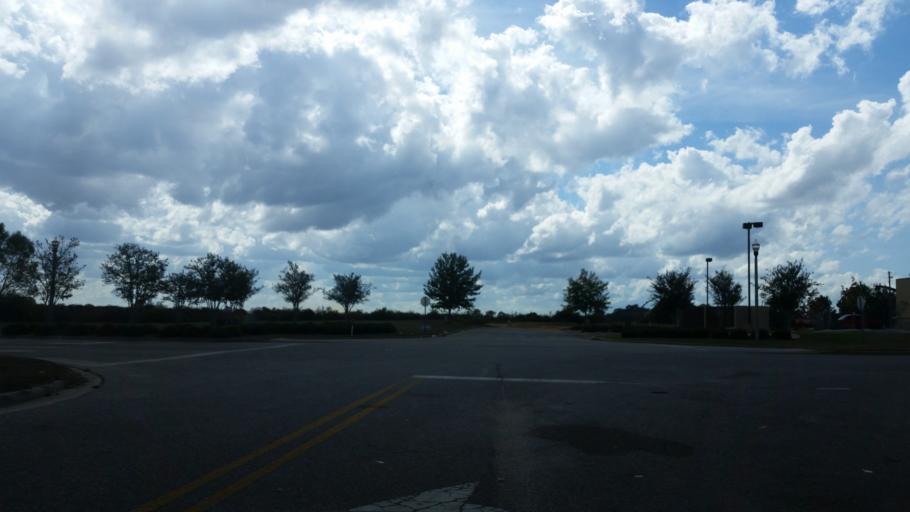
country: US
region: Alabama
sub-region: Escambia County
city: Atmore
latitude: 31.1058
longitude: -87.4756
